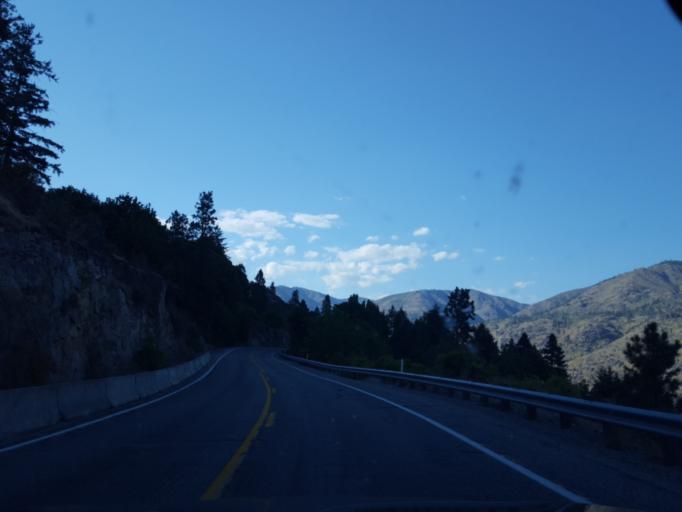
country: US
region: Washington
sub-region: Chelan County
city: Granite Falls
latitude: 47.9547
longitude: -120.2095
